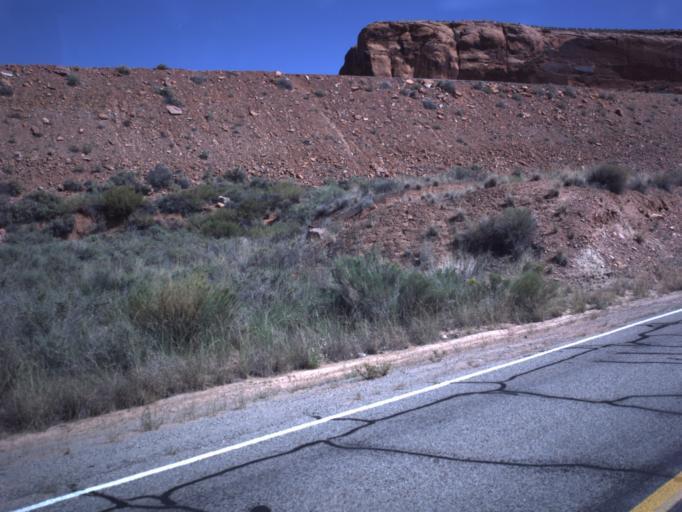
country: US
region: Utah
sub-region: Grand County
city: Moab
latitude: 38.5764
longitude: -109.6340
